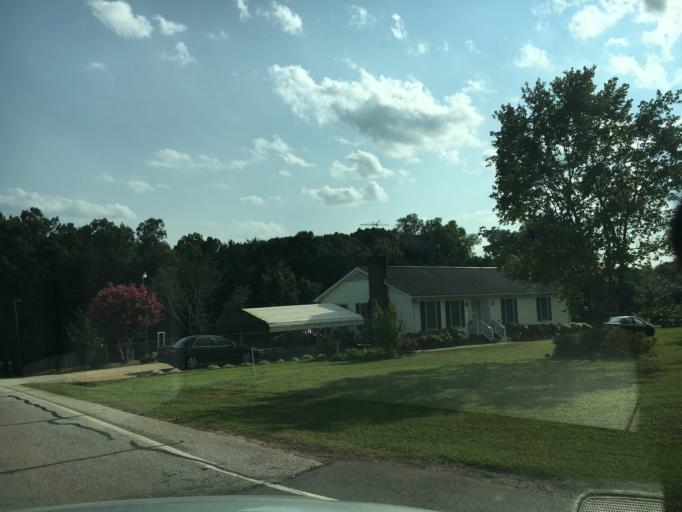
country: US
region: South Carolina
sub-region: Greenville County
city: Taylors
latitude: 34.9781
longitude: -82.2967
